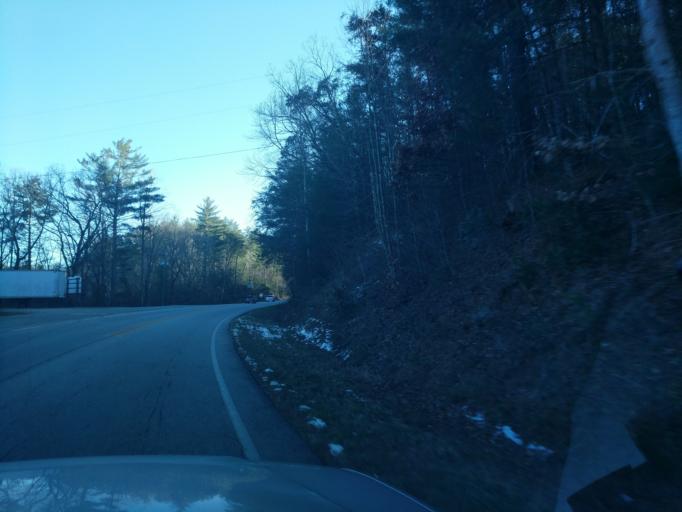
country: US
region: Georgia
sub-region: Rabun County
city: Clayton
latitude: 34.8543
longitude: -83.3648
